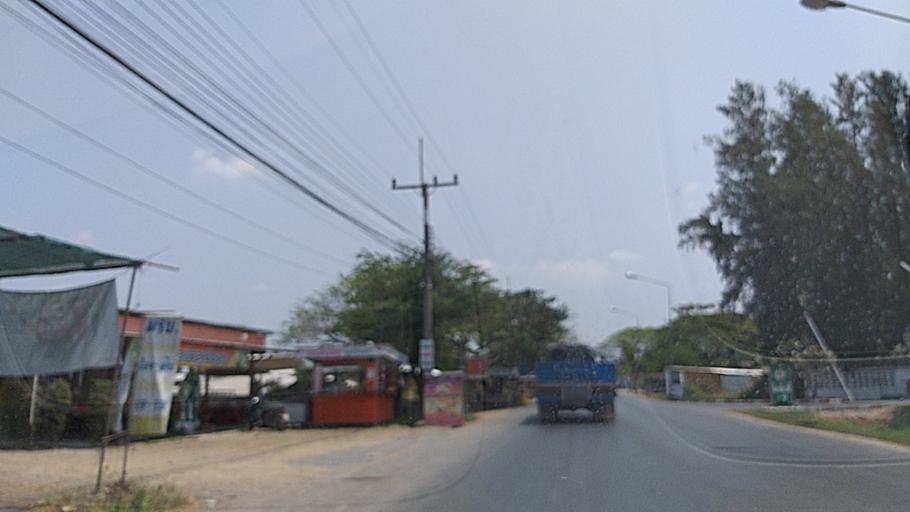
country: TH
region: Bangkok
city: Nong Chok
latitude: 13.9715
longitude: 100.9619
